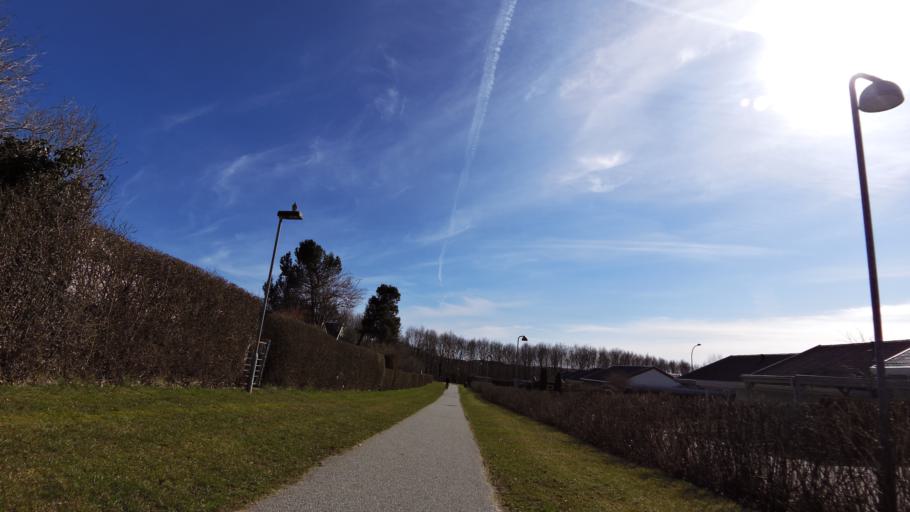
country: DK
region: Central Jutland
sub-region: Arhus Kommune
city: Stavtrup
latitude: 56.1747
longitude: 10.1040
